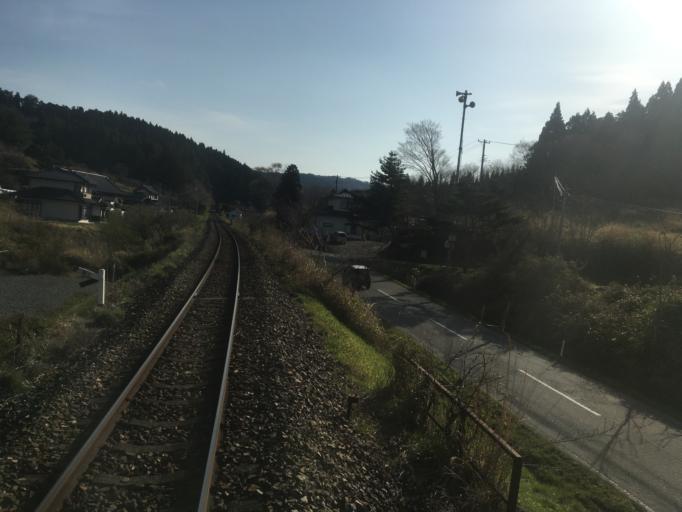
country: JP
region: Iwate
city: Ofunato
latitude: 39.0558
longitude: 141.8047
